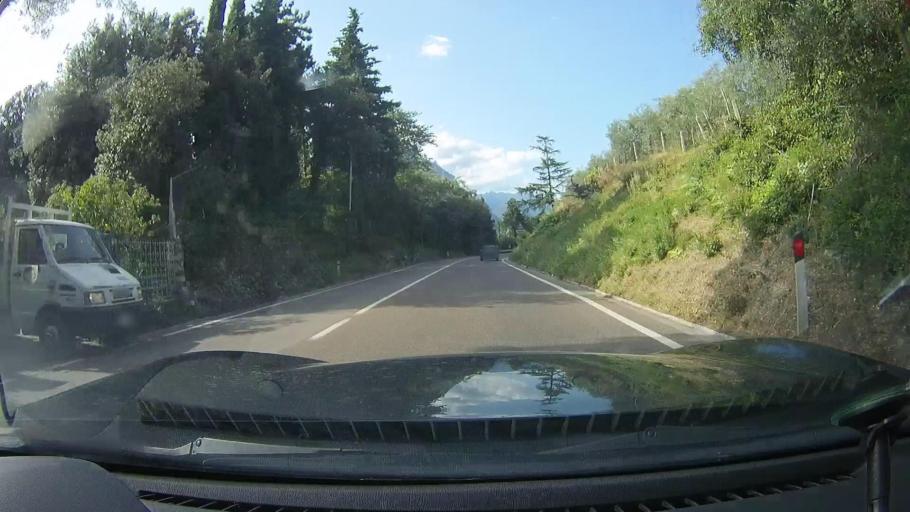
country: IT
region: Trentino-Alto Adige
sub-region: Provincia di Trento
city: Torbole sul Garda
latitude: 45.8353
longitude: 10.8597
